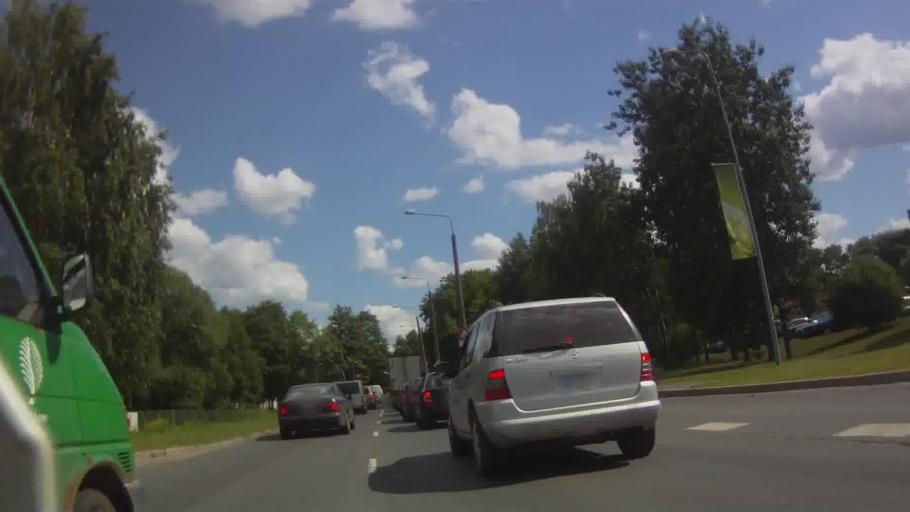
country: LV
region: Riga
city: Riga
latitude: 56.9150
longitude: 24.1208
